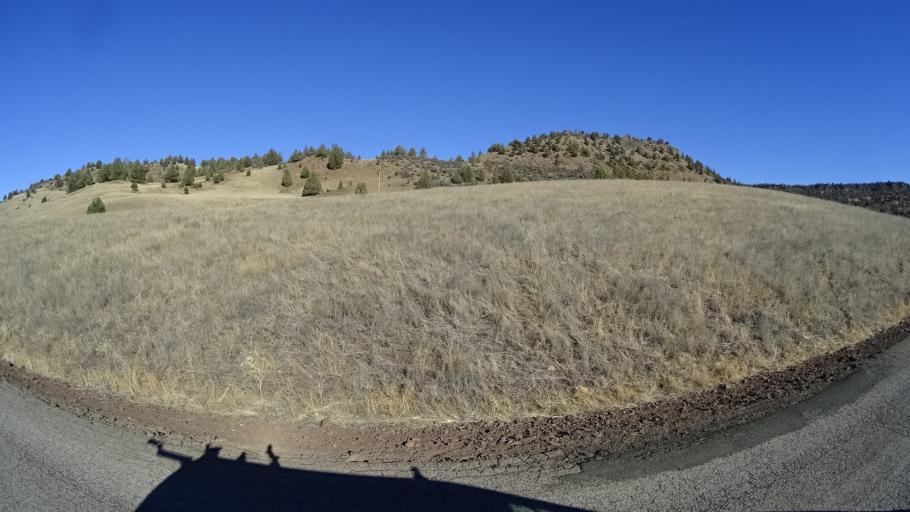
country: US
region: California
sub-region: Siskiyou County
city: Montague
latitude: 41.9681
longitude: -122.4203
